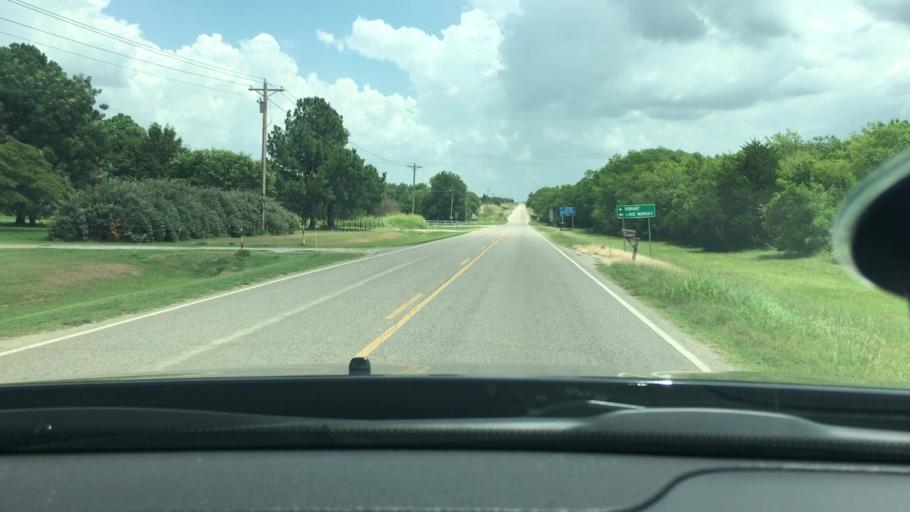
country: US
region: Oklahoma
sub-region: Love County
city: Marietta
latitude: 33.9404
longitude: -97.0939
